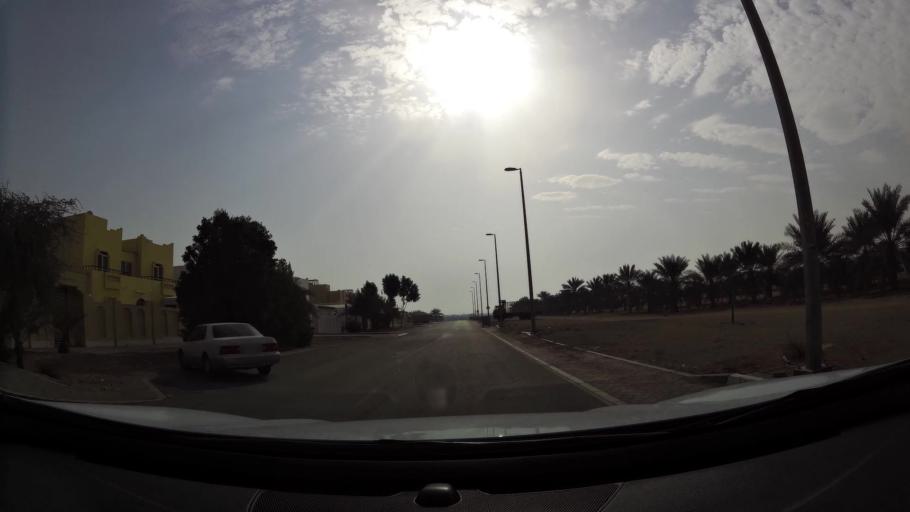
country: AE
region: Abu Dhabi
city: Abu Dhabi
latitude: 24.2375
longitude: 54.7236
